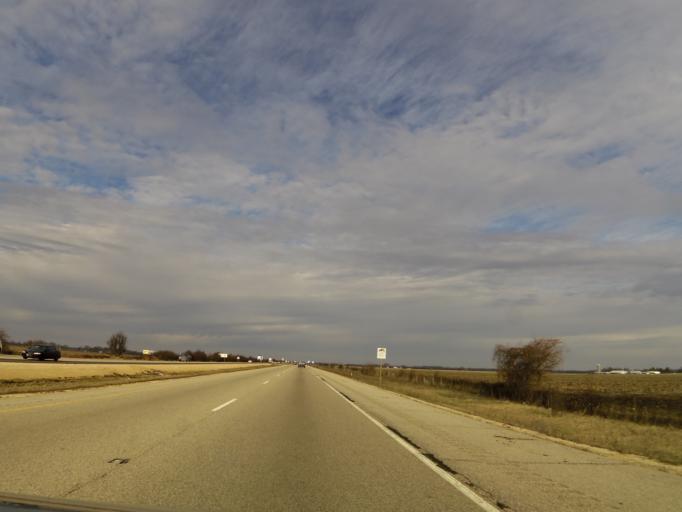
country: US
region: Wisconsin
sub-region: Rock County
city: Janesville
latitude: 42.6414
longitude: -88.9829
